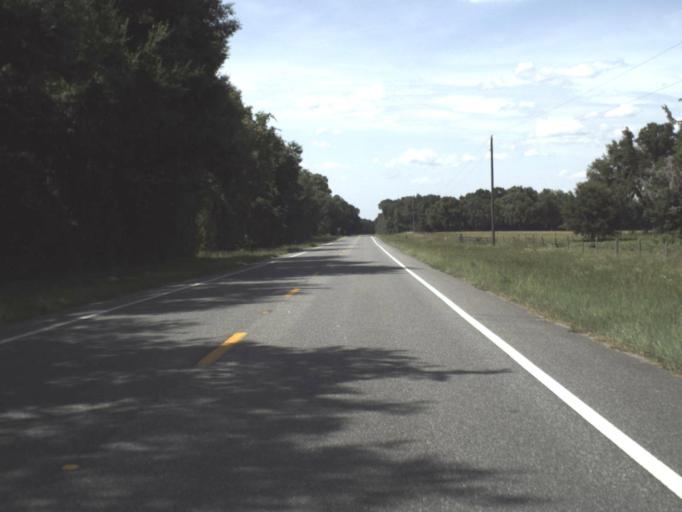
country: US
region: Florida
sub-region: Alachua County
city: High Springs
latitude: 29.8473
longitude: -82.7418
